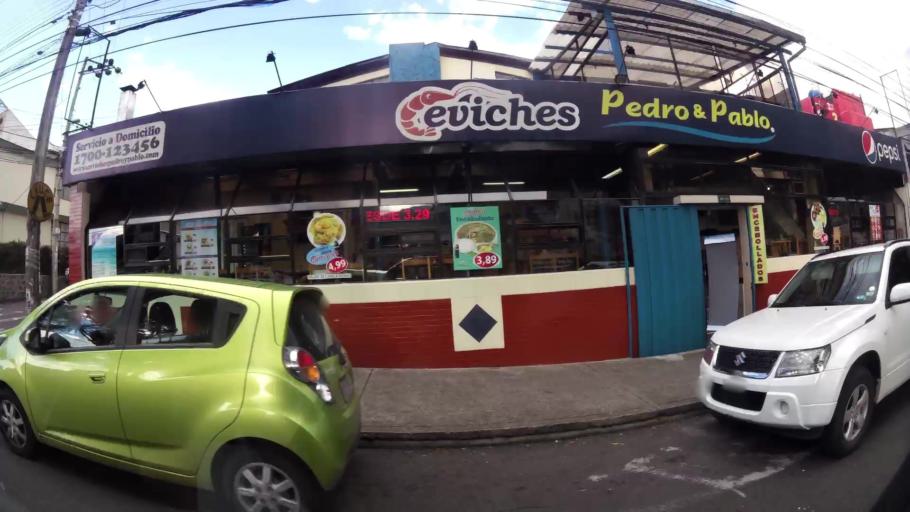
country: EC
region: Pichincha
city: Quito
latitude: -0.1271
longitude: -78.4869
